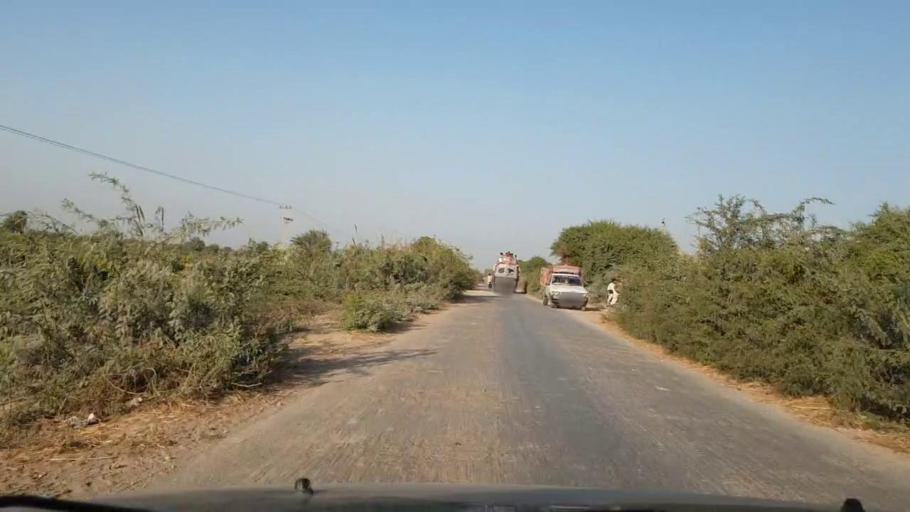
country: PK
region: Sindh
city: Chambar
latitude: 25.2766
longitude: 68.8065
